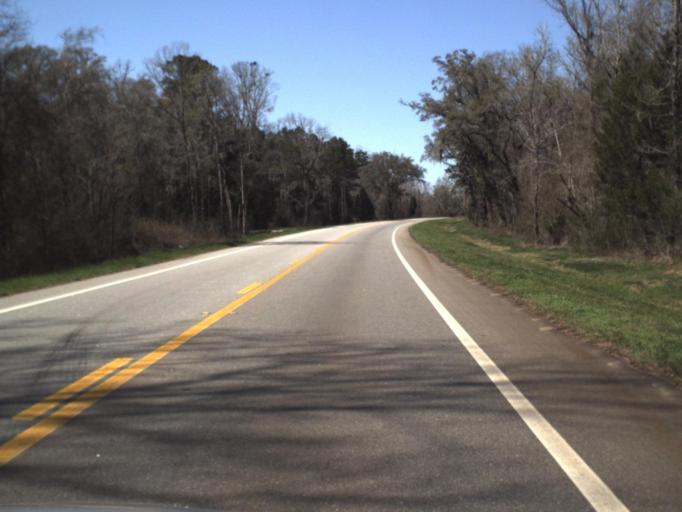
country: US
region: Florida
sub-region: Jackson County
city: Marianna
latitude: 30.8212
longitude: -85.3233
